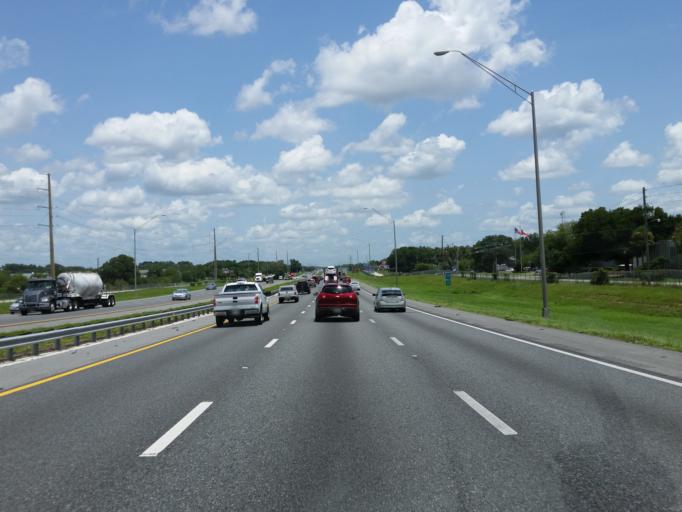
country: US
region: Florida
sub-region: Marion County
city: Ocala
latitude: 29.1708
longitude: -82.1847
